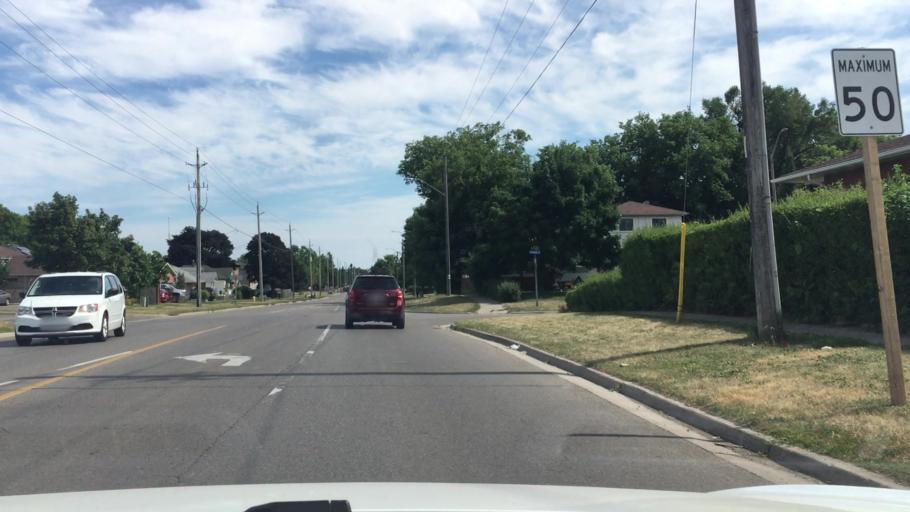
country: CA
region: Ontario
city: Oshawa
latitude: 43.9060
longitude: -78.8132
